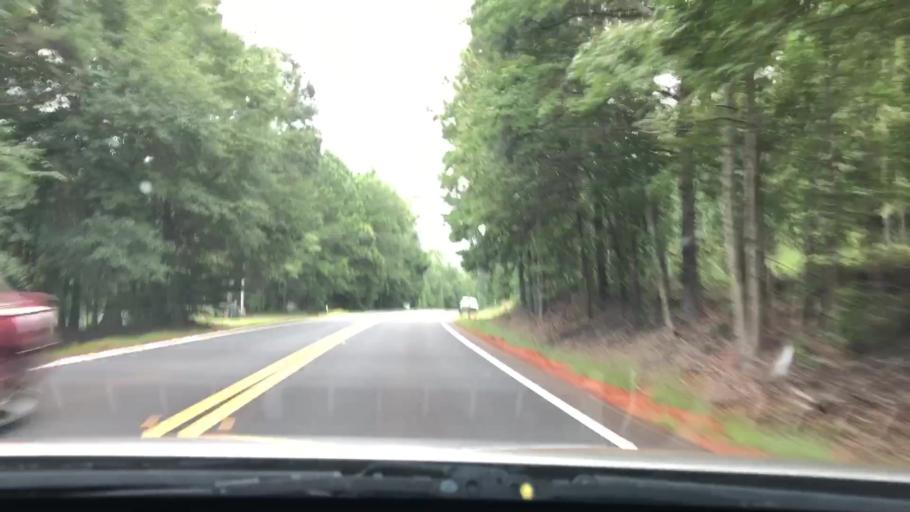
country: US
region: Georgia
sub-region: Upson County
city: Hannahs Mill
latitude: 33.0157
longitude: -84.4125
